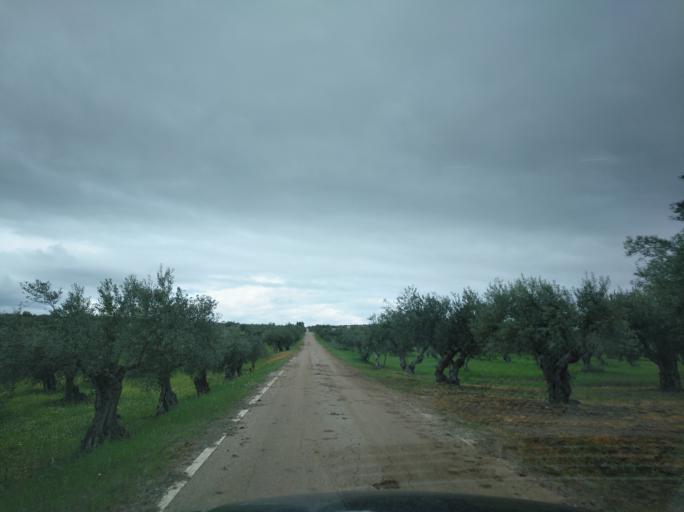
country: PT
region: Portalegre
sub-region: Campo Maior
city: Campo Maior
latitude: 38.9815
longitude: -7.0337
